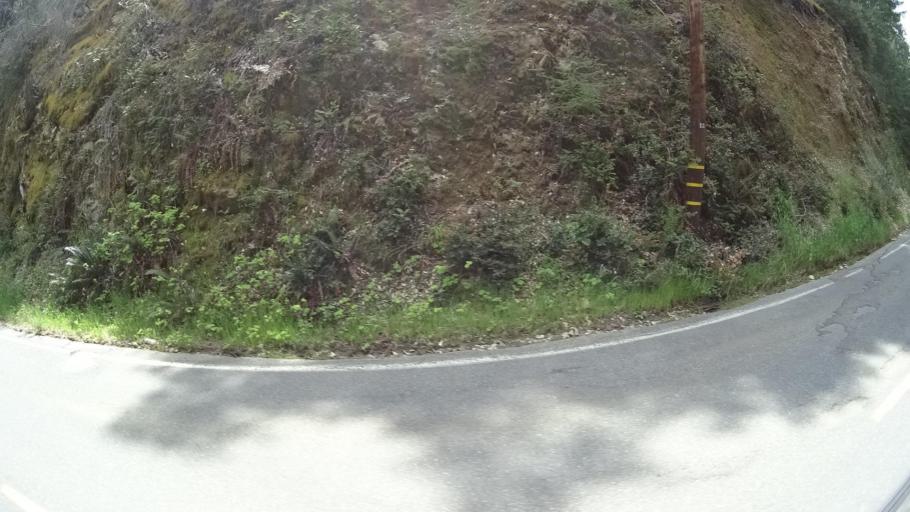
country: US
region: California
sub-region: Humboldt County
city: Redway
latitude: 40.0541
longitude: -123.9874
